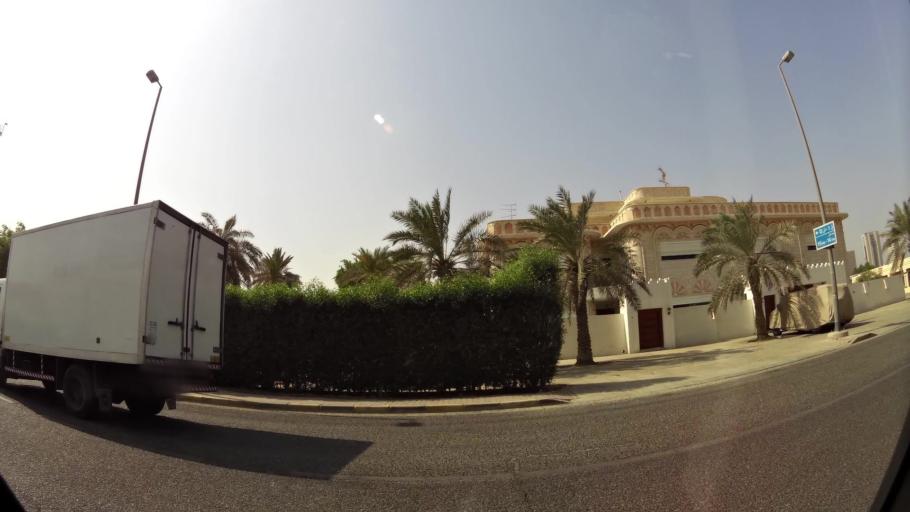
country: KW
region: Al Asimah
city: Ad Dasmah
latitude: 29.3602
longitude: 47.9940
